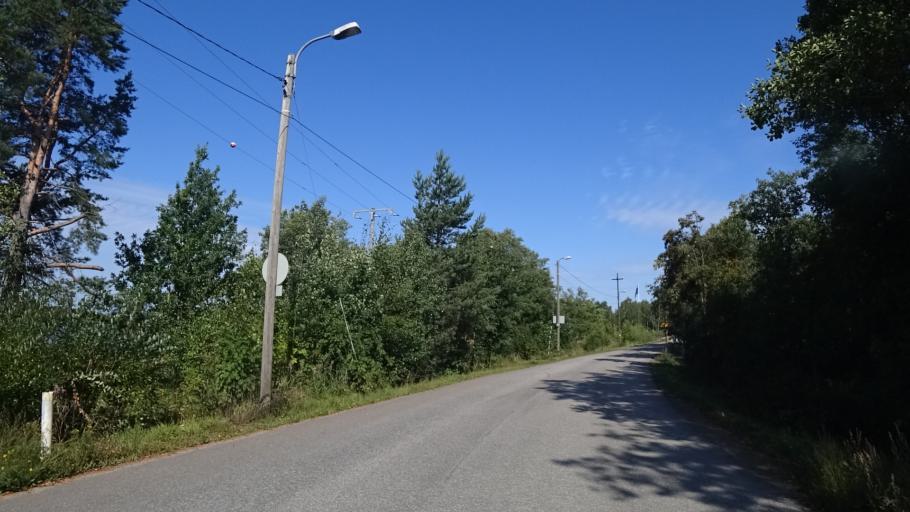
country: FI
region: Kymenlaakso
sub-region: Kotka-Hamina
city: Hamina
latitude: 60.5540
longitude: 27.1996
